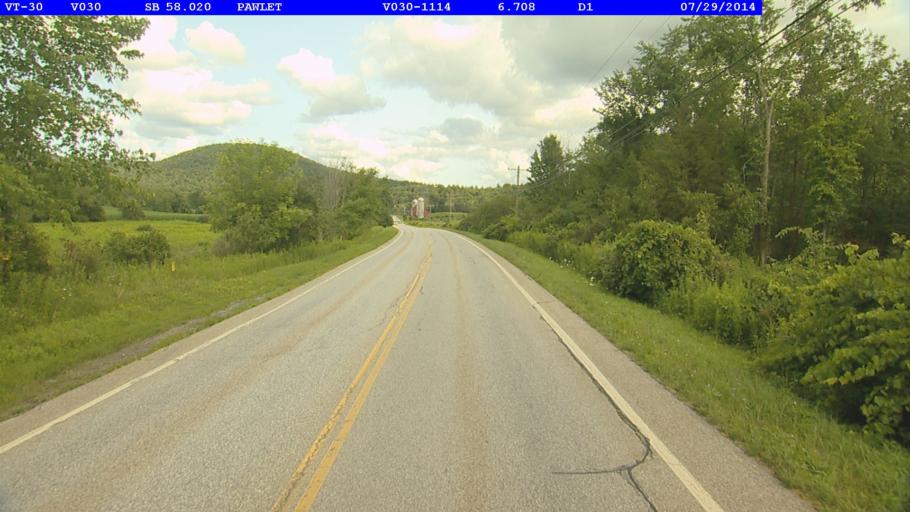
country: US
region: New York
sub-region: Washington County
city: Granville
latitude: 43.3872
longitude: -73.2178
